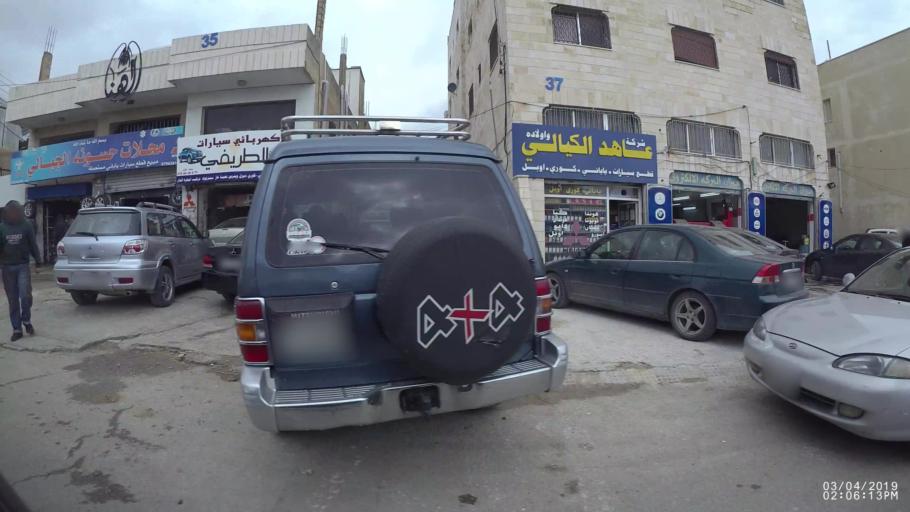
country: JO
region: Amman
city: Wadi as Sir
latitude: 31.9421
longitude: 35.8431
